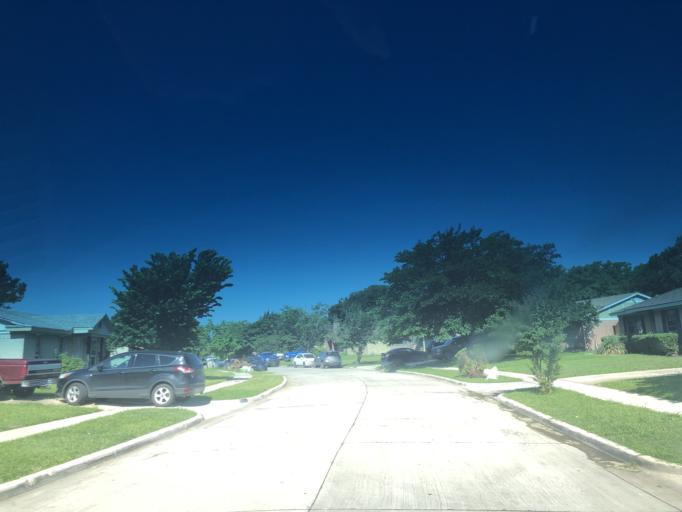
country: US
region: Texas
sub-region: Dallas County
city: Grand Prairie
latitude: 32.7142
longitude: -97.0079
